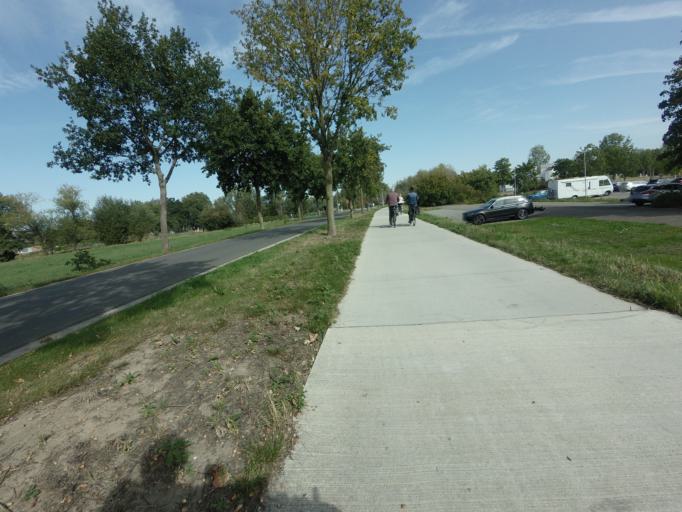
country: BE
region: Flanders
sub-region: Provincie Limburg
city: Maaseik
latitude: 51.1317
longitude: 5.8147
